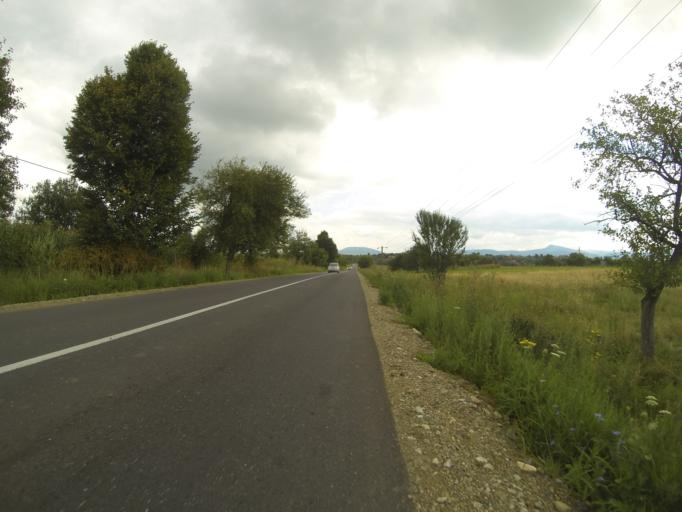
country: RO
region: Brasov
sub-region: Comuna Parau
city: Parau
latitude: 45.8479
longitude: 25.1780
